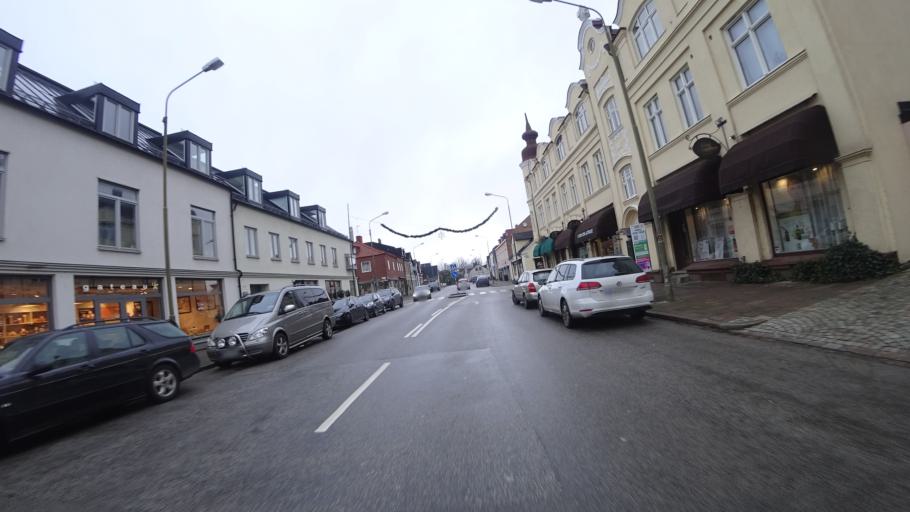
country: SE
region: Skane
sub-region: Malmo
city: Bunkeflostrand
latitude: 55.5840
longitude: 12.9319
